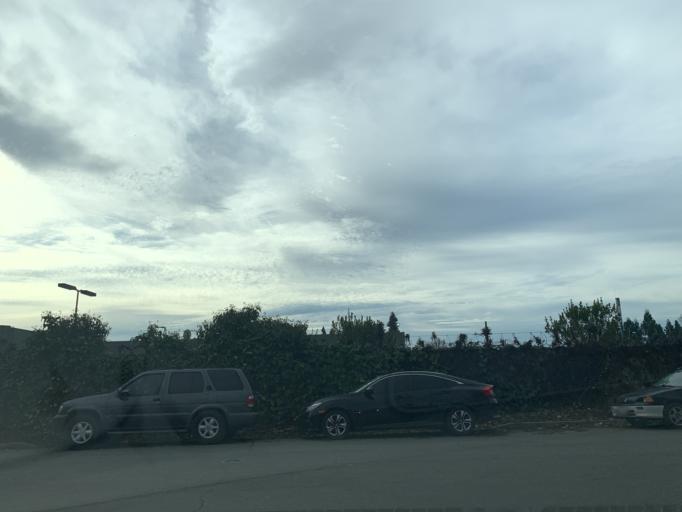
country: US
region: California
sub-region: Santa Clara County
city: Buena Vista
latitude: 37.3187
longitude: -121.9169
